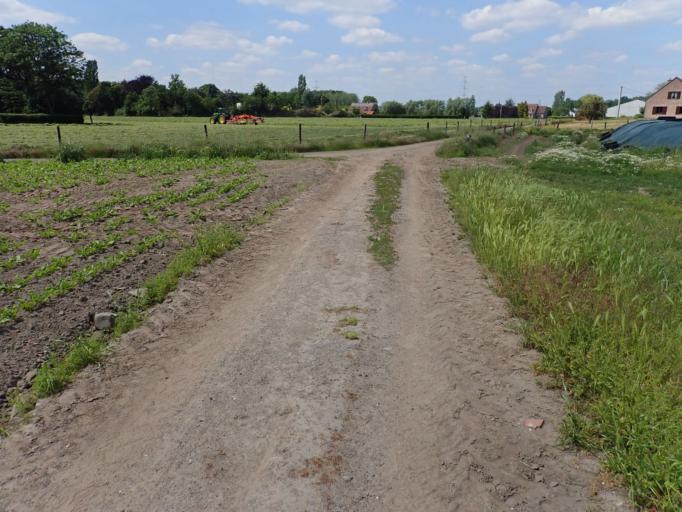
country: BE
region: Flanders
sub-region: Provincie Vlaams-Brabant
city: Londerzeel
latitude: 51.0173
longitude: 4.3087
